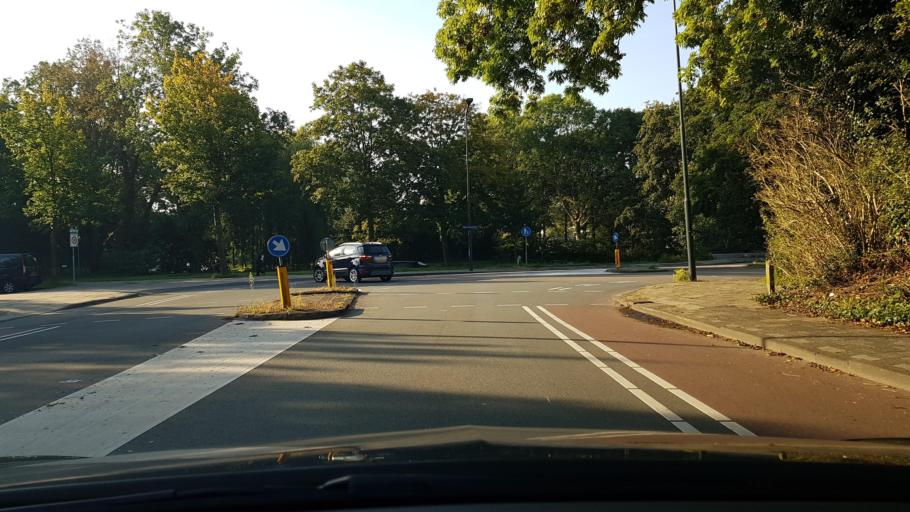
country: NL
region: North Holland
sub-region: Gemeente Haarlem
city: Haarlem
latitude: 52.3546
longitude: 4.6573
